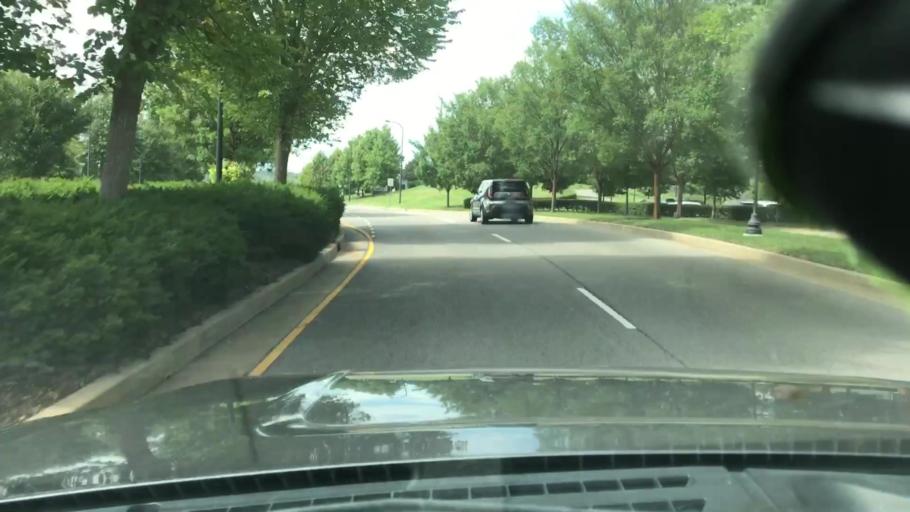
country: US
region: Tennessee
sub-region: Williamson County
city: Franklin
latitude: 35.9381
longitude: -86.8298
